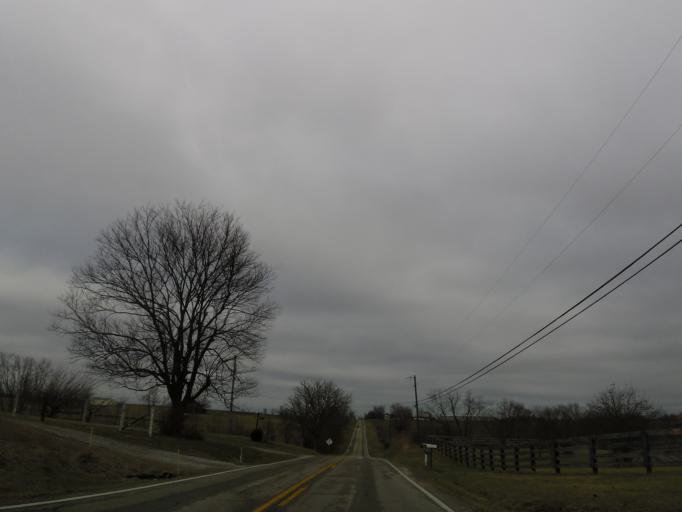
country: US
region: Kentucky
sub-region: Henry County
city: Eminence
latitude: 38.3411
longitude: -85.0778
